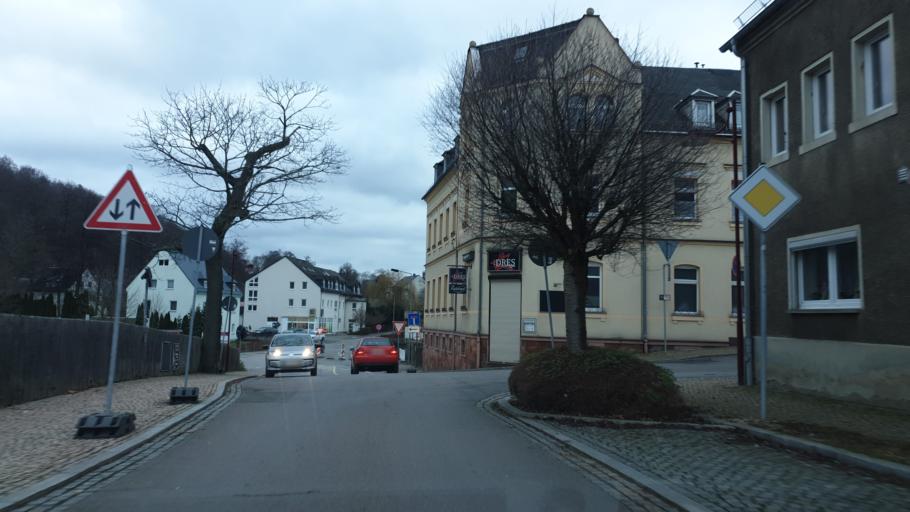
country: DE
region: Saxony
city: Lichtenstein
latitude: 50.7525
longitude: 12.6341
